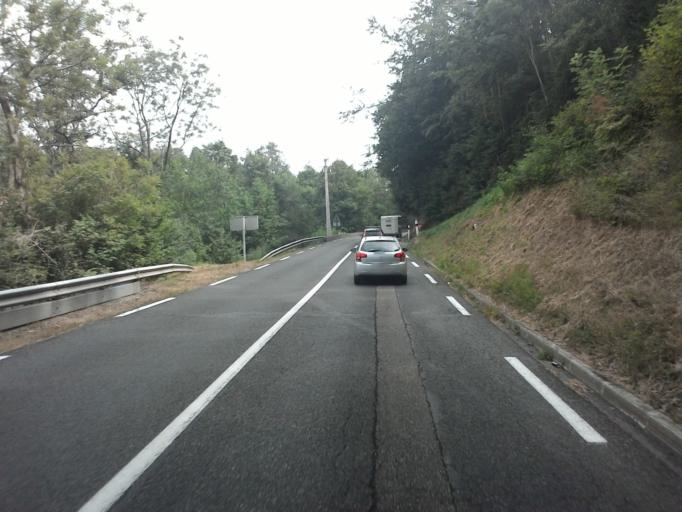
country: FR
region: Rhone-Alpes
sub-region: Departement de l'Isere
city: Notre-Dame-de-Mesage
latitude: 45.0297
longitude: 5.7714
